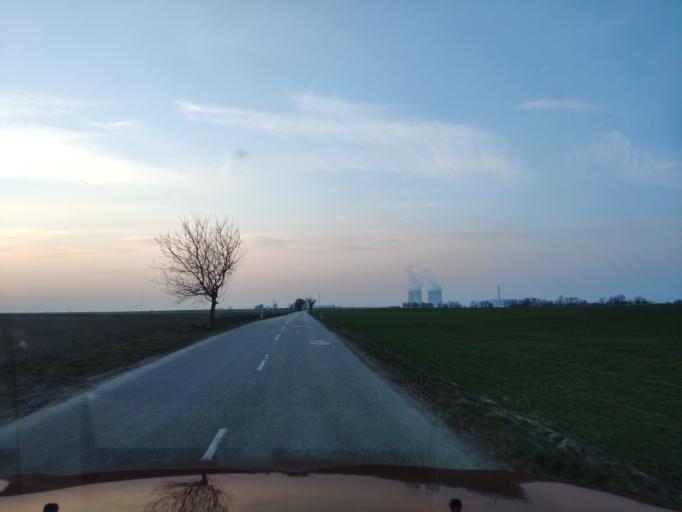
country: SK
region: Trnavsky
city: Leopoldov
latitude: 48.4720
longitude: 17.7139
